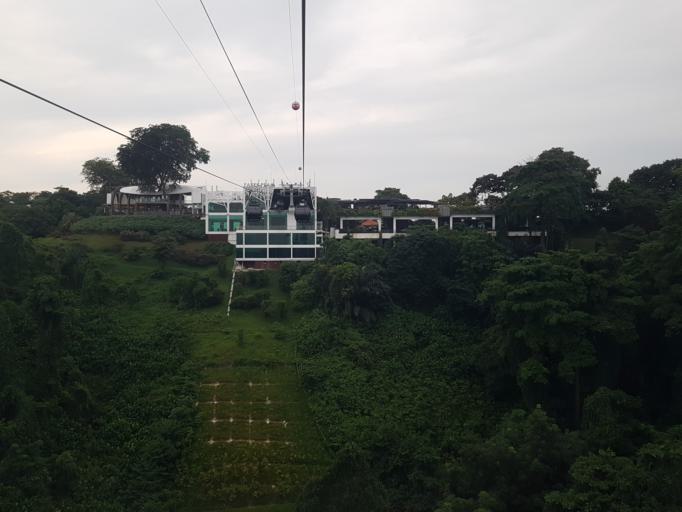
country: SG
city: Singapore
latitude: 1.2698
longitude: 103.8193
